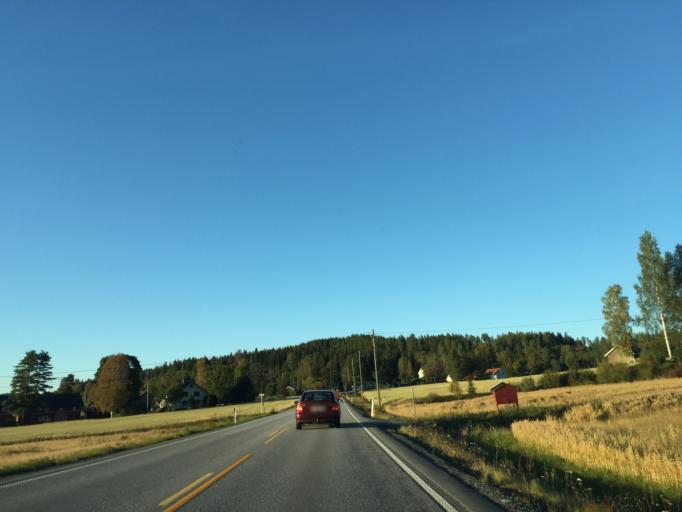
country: NO
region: Hedmark
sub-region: Nord-Odal
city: Sand
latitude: 60.4084
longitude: 11.5191
